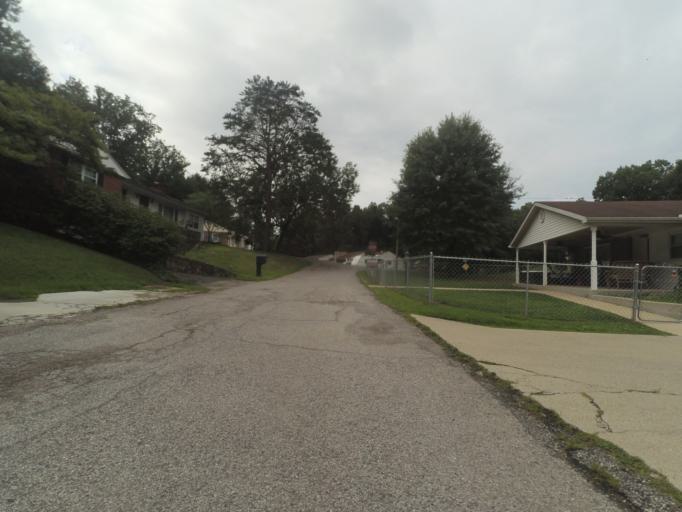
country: US
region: West Virginia
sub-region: Cabell County
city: Huntington
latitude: 38.3981
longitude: -82.4010
